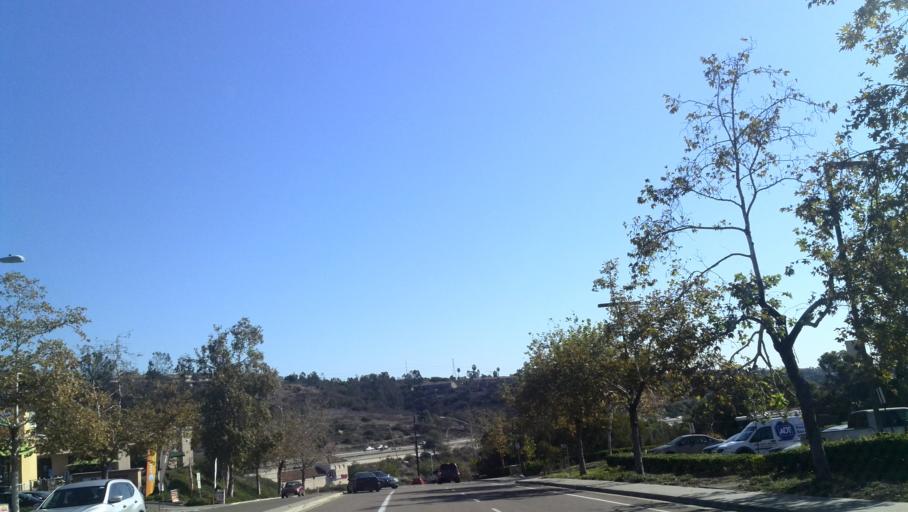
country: US
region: California
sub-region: San Diego County
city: La Mesa
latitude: 32.8089
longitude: -117.1162
